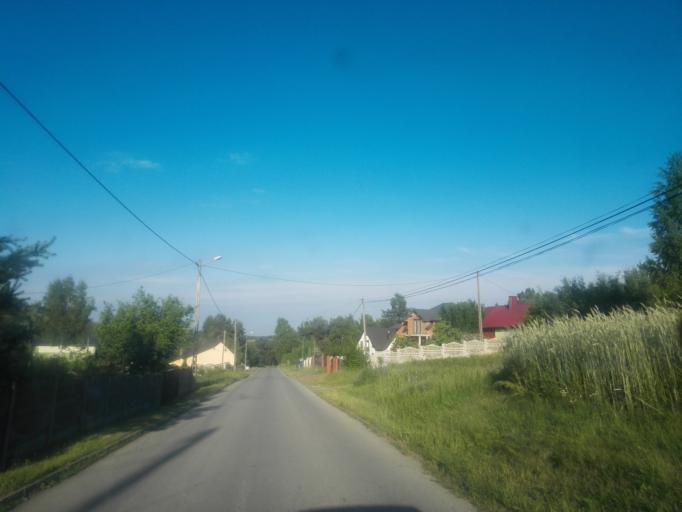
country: PL
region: Silesian Voivodeship
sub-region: Powiat czestochowski
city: Potok Zloty
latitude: 50.6925
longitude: 19.3704
